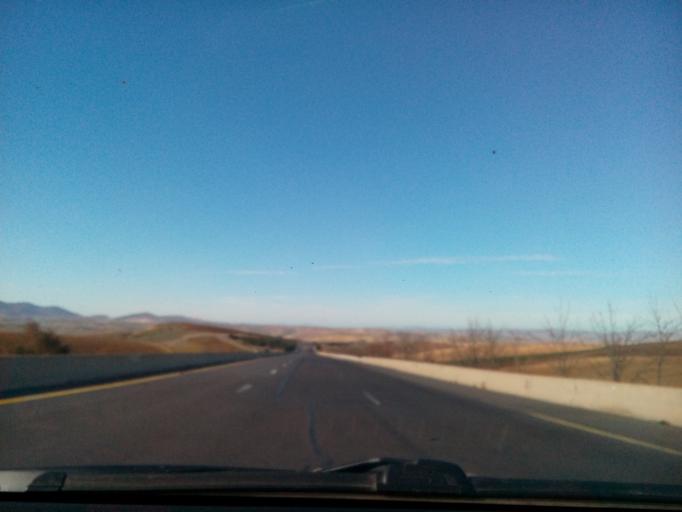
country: DZ
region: Tlemcen
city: Ouled Mimoun
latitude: 35.0293
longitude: -1.0061
